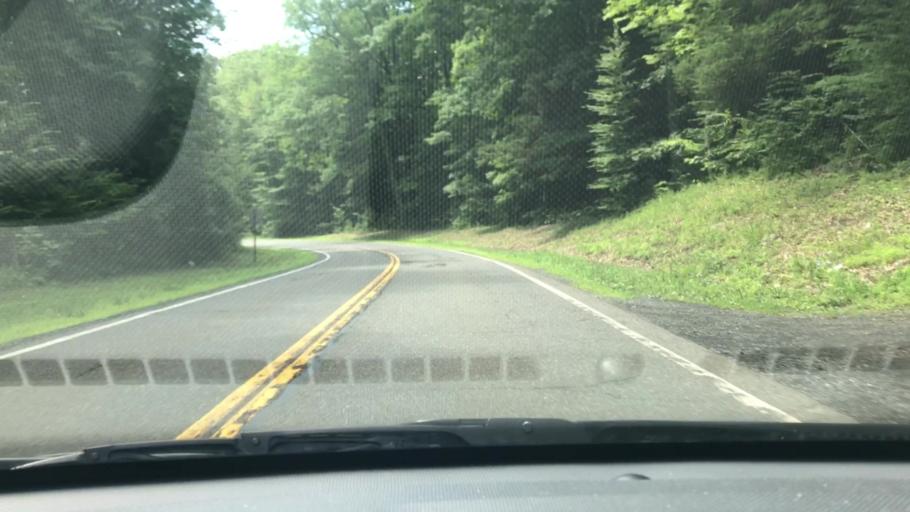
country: US
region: New York
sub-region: Ulster County
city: Shokan
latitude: 41.9677
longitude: -74.2102
